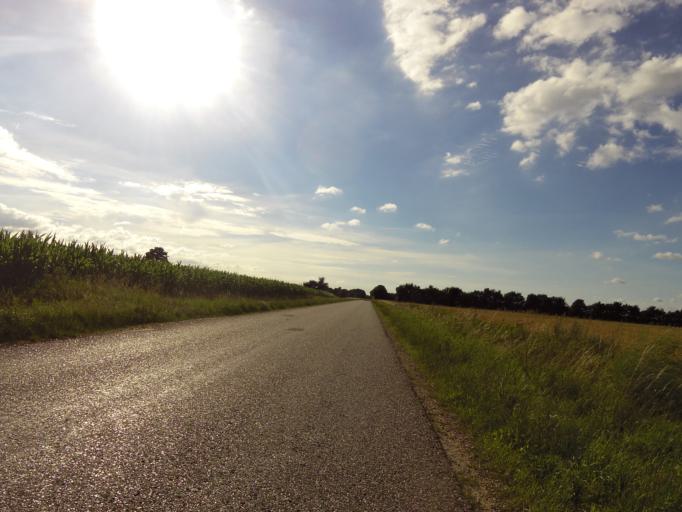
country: DK
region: South Denmark
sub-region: Haderslev Kommune
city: Vojens
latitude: 55.2024
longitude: 9.2862
